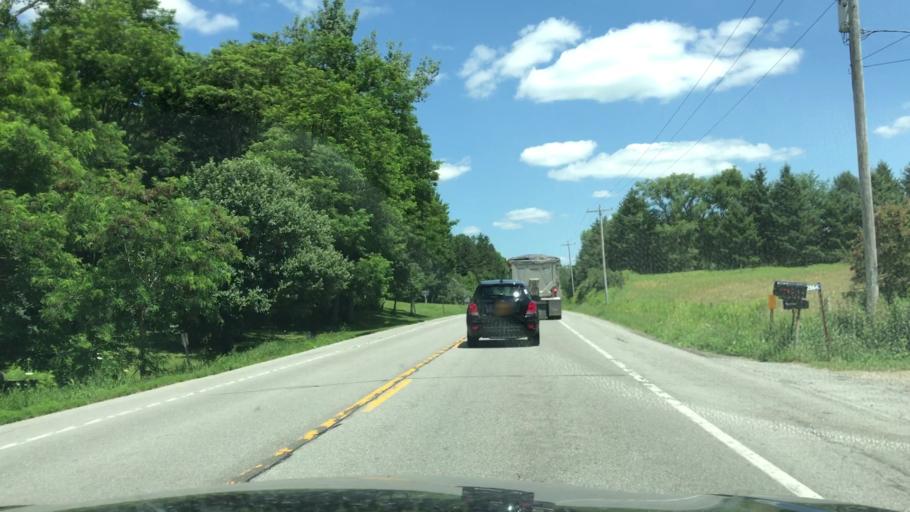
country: US
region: New York
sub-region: Wyoming County
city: Attica
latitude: 42.7556
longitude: -78.2899
